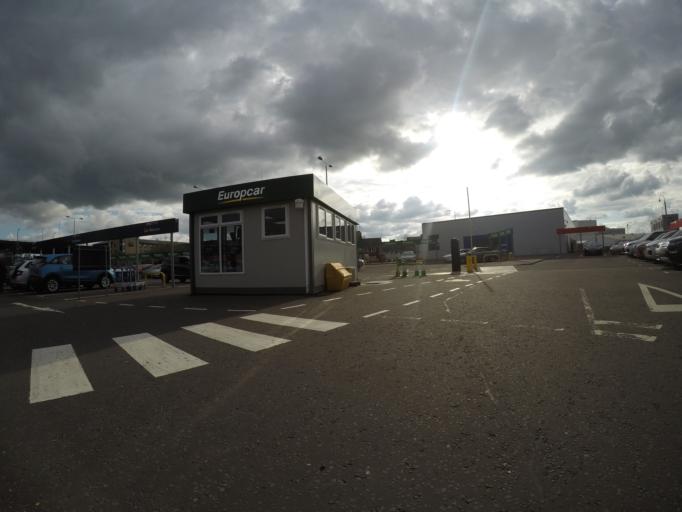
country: GB
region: Scotland
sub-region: Renfrewshire
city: Inchinnan
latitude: 55.8646
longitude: -4.4272
